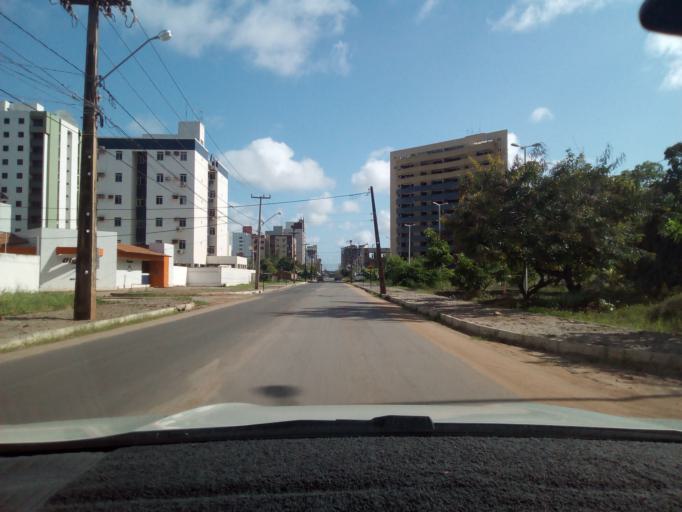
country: BR
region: Paraiba
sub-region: Cabedelo
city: Cabedelo
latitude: -7.0404
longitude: -34.8431
